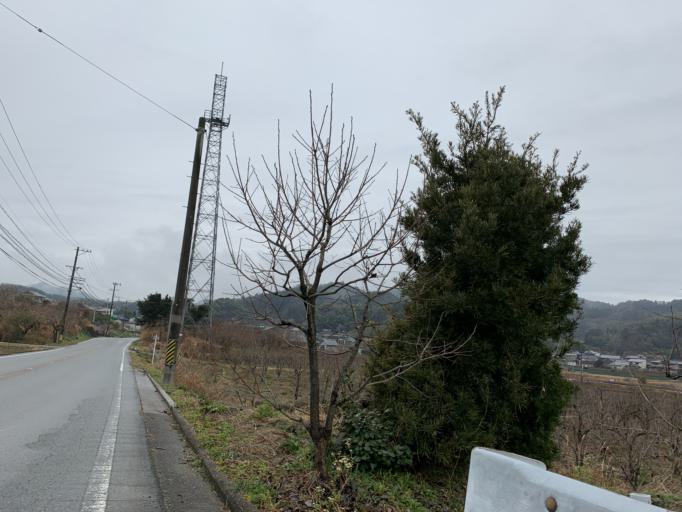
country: JP
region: Mie
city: Ise
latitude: 34.4779
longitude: 136.5444
